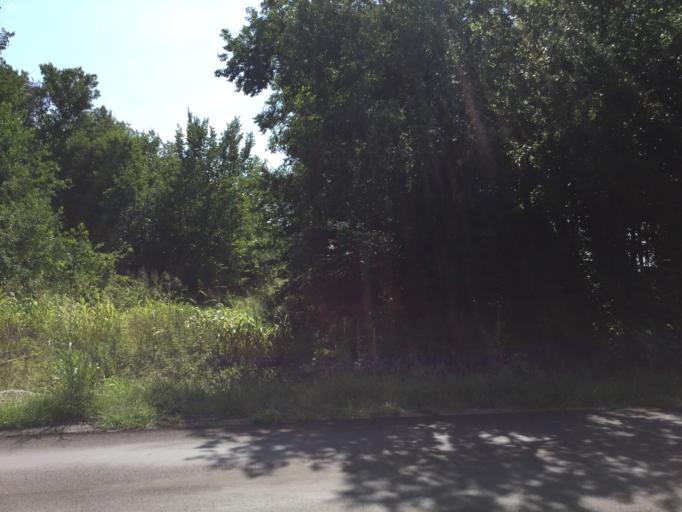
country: US
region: Kansas
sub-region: Montgomery County
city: Coffeyville
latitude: 37.0308
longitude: -95.5775
